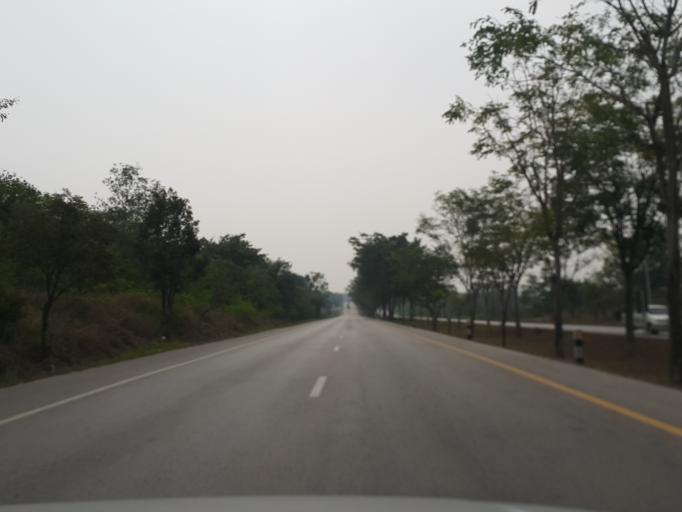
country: TH
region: Lampang
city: Ko Kha
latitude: 18.1402
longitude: 99.3908
